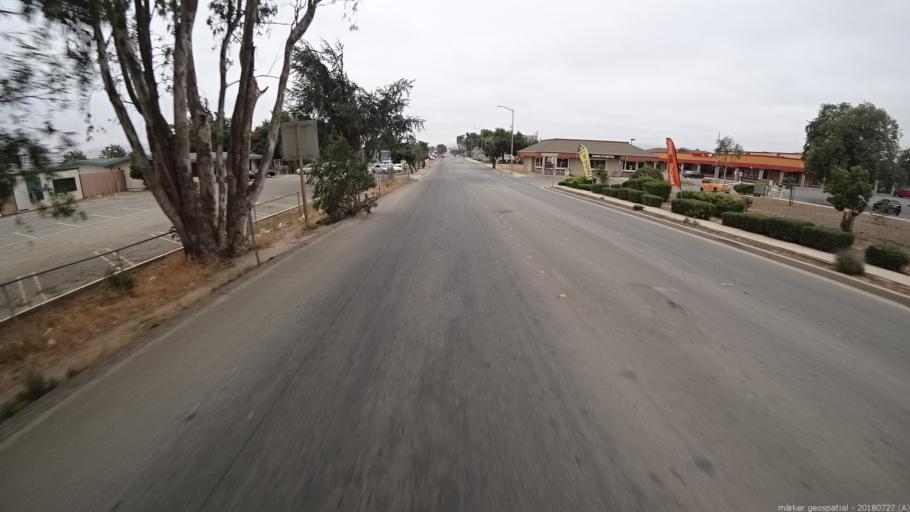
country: US
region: California
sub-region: Monterey County
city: Greenfield
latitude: 36.3284
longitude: -121.2457
